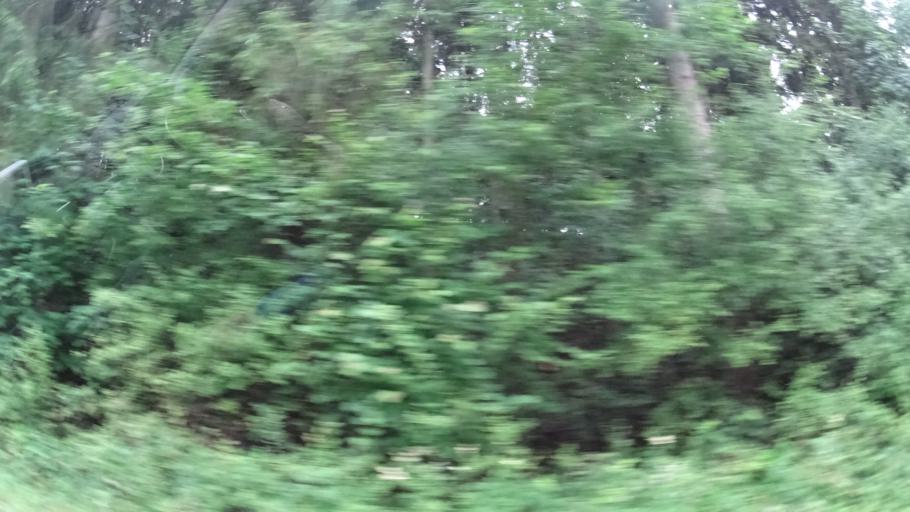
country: BE
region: Wallonia
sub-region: Province du Luxembourg
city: Daverdisse
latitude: 49.9932
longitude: 5.0705
